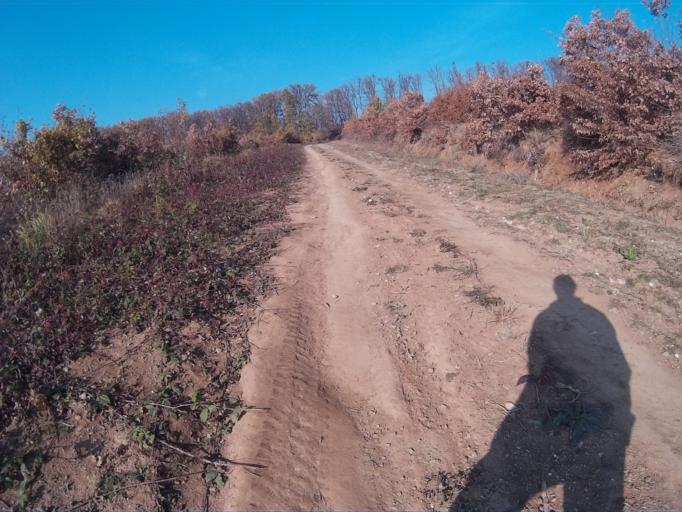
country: HU
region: Heves
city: Felsotarkany
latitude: 48.0109
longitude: 20.3981
